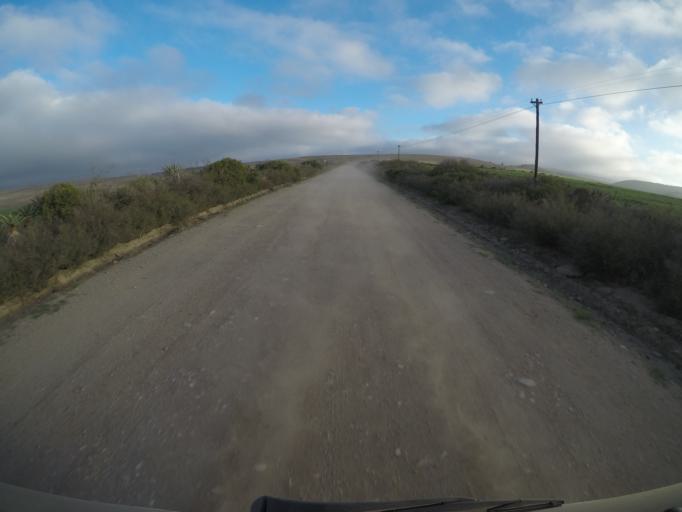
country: ZA
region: Western Cape
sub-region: Eden District Municipality
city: Mossel Bay
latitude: -34.1208
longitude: 22.0534
